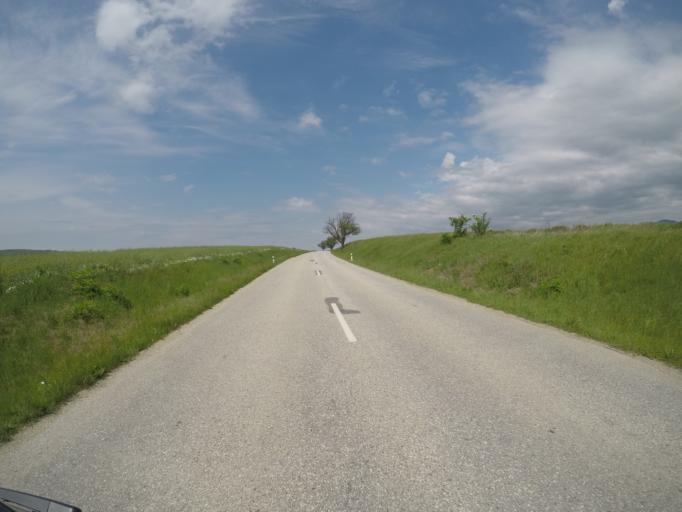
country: HU
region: Komarom-Esztergom
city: Esztergom
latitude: 47.9065
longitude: 18.7547
